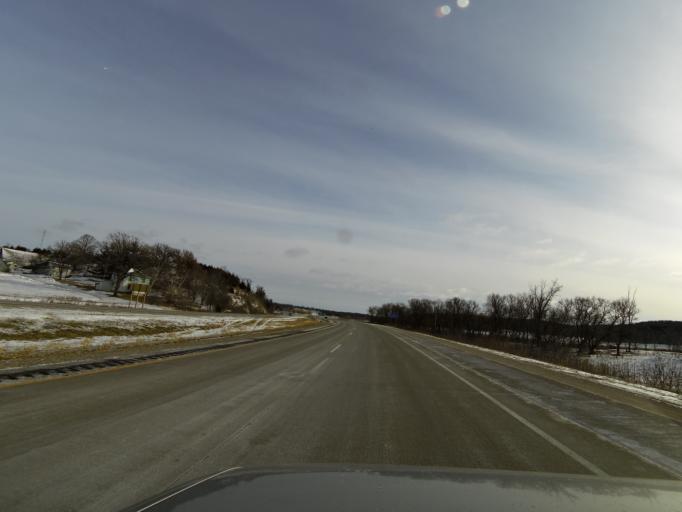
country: US
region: Wisconsin
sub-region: Pierce County
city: River Falls
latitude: 44.9038
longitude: -92.6568
